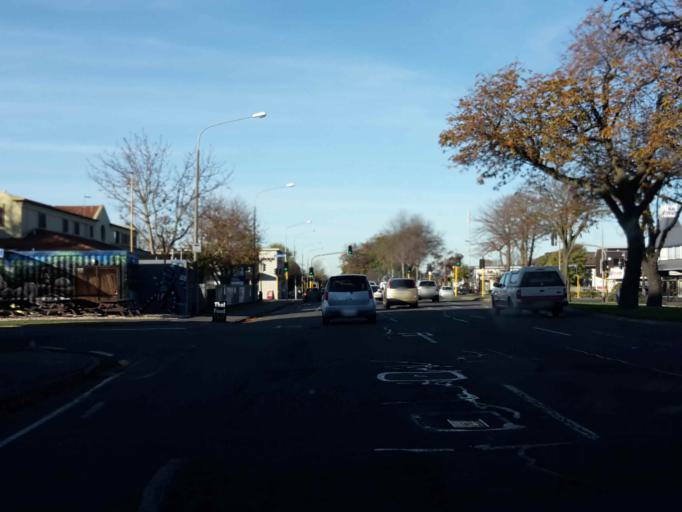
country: NZ
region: Canterbury
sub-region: Christchurch City
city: Christchurch
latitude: -43.5208
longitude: 172.6352
